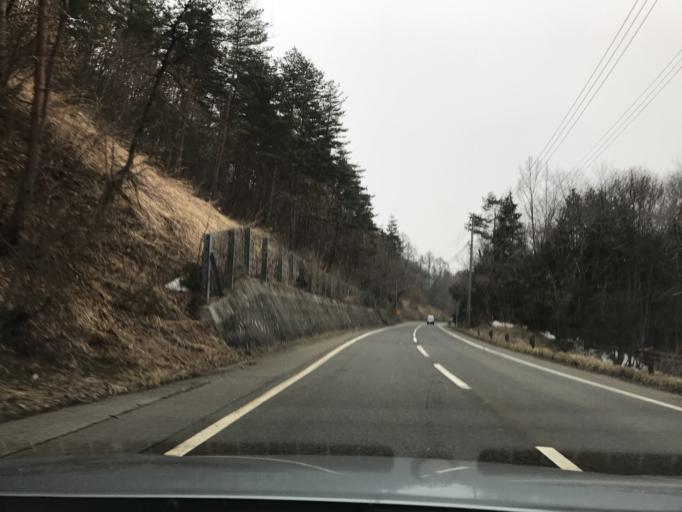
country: JP
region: Nagano
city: Omachi
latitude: 36.5342
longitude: 137.8646
